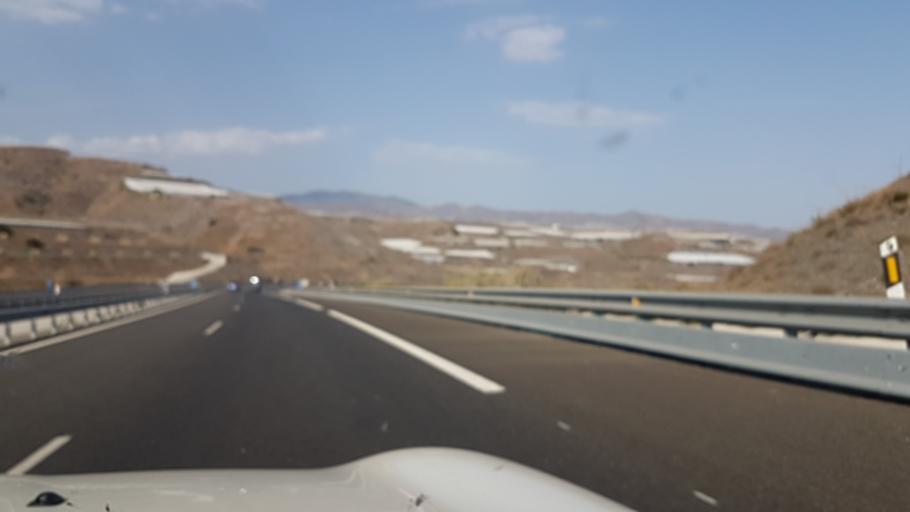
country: ES
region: Andalusia
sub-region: Provincia de Granada
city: Albunol
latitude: 36.7518
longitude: -3.2071
